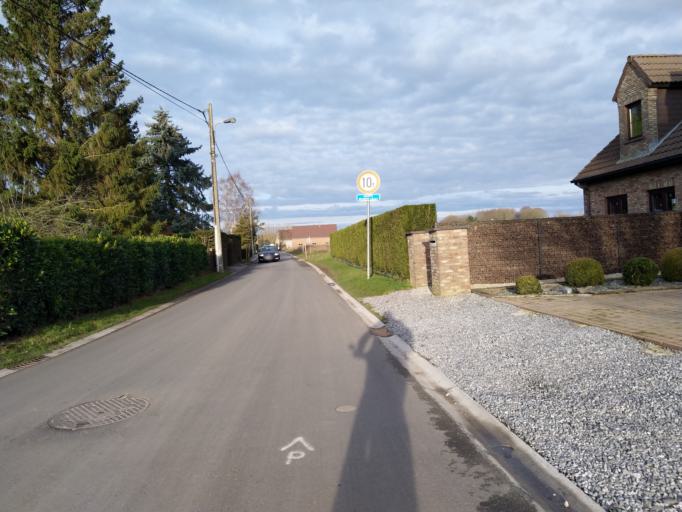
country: BE
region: Wallonia
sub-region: Province du Hainaut
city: Mons
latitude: 50.5167
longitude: 4.0023
